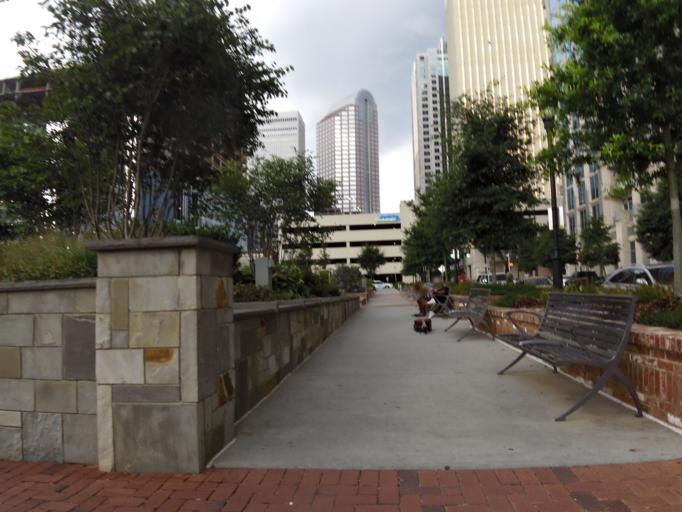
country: US
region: North Carolina
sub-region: Mecklenburg County
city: Charlotte
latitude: 35.2265
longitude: -80.8481
